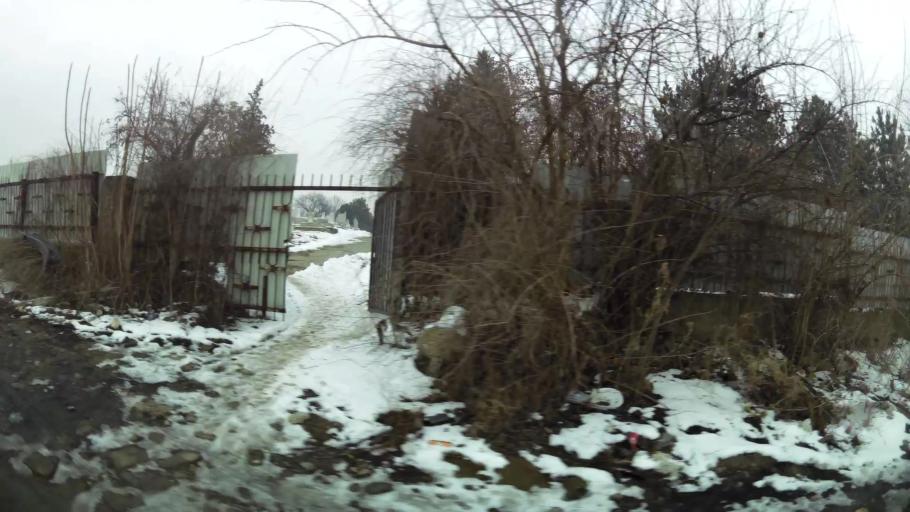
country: MK
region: Suto Orizari
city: Suto Orizare
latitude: 42.0351
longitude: 21.4328
